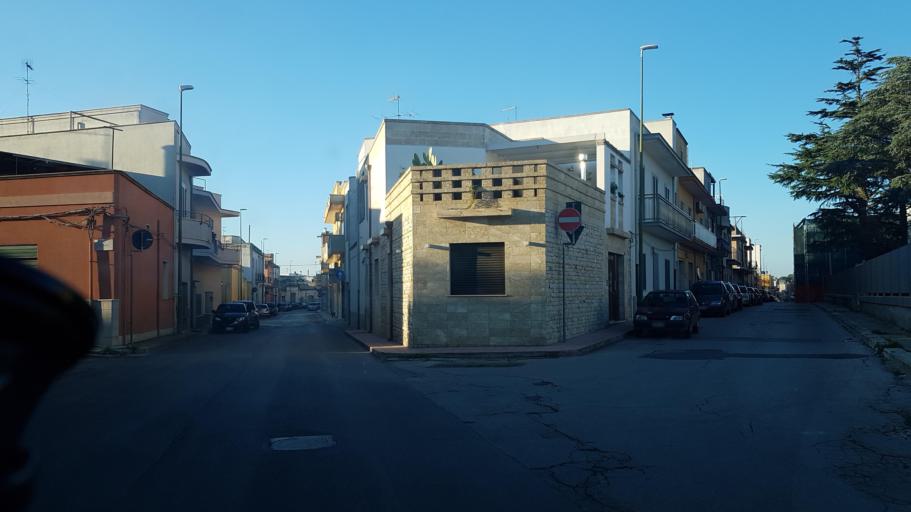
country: IT
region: Apulia
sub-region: Provincia di Brindisi
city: Latiano
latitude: 40.5492
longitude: 17.7218
